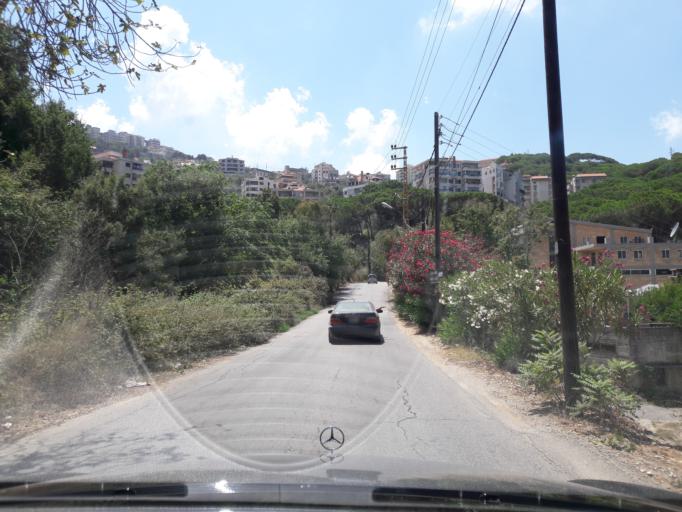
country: LB
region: Mont-Liban
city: Djounie
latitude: 33.9260
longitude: 35.6608
